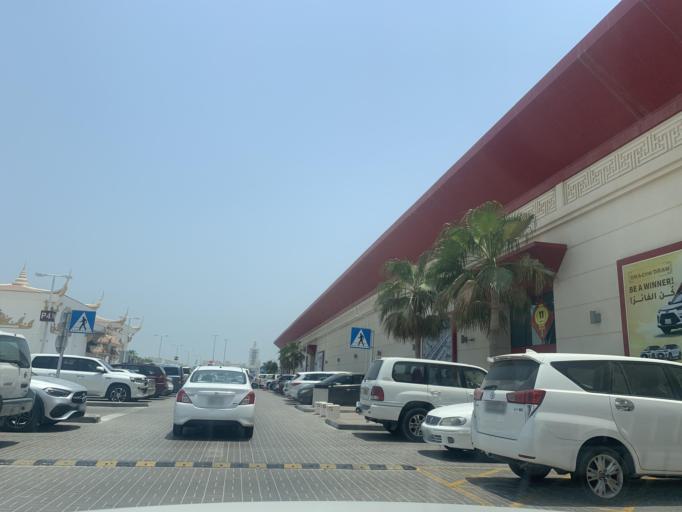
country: BH
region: Muharraq
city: Al Muharraq
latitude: 26.3059
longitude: 50.6256
